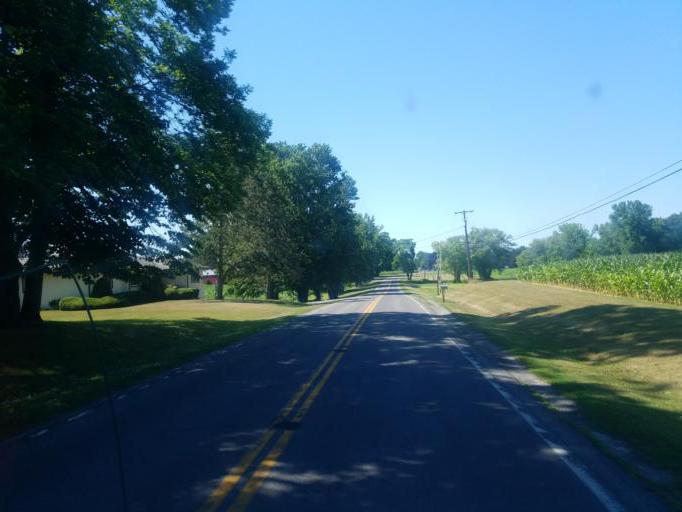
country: US
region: New York
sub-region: Ontario County
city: Geneva
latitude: 42.9232
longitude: -76.9973
